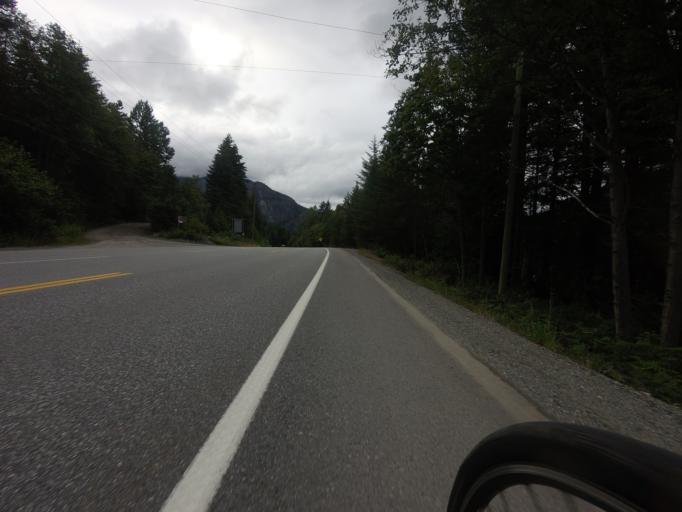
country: CA
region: British Columbia
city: Whistler
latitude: 50.2084
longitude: -122.8828
